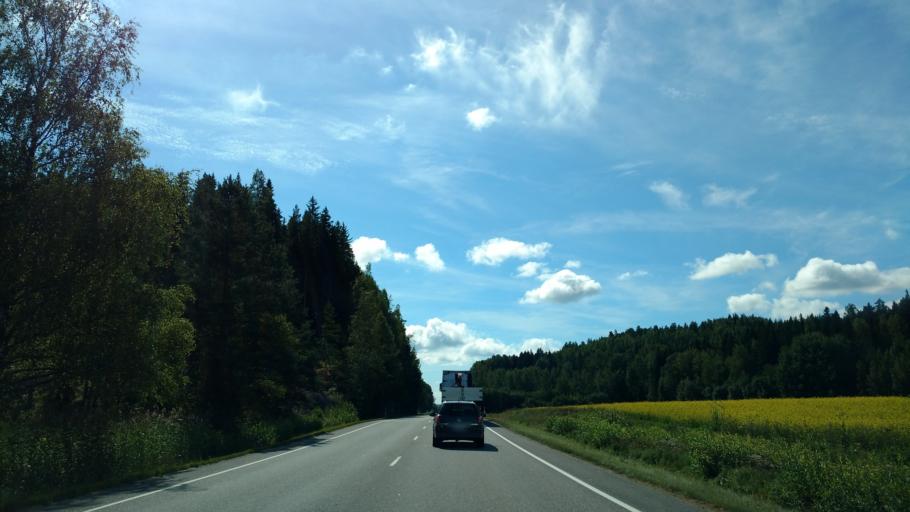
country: FI
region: Varsinais-Suomi
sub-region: Salo
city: Salo
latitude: 60.3127
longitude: 23.0993
